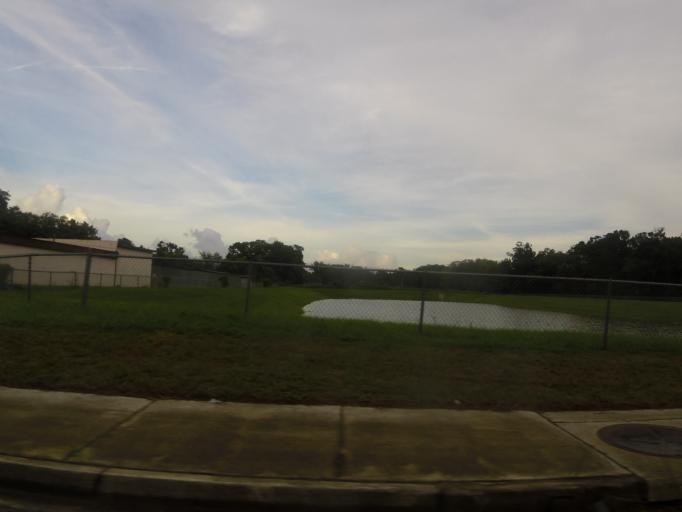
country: US
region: Florida
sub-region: Duval County
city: Jacksonville
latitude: 30.3391
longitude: -81.7055
